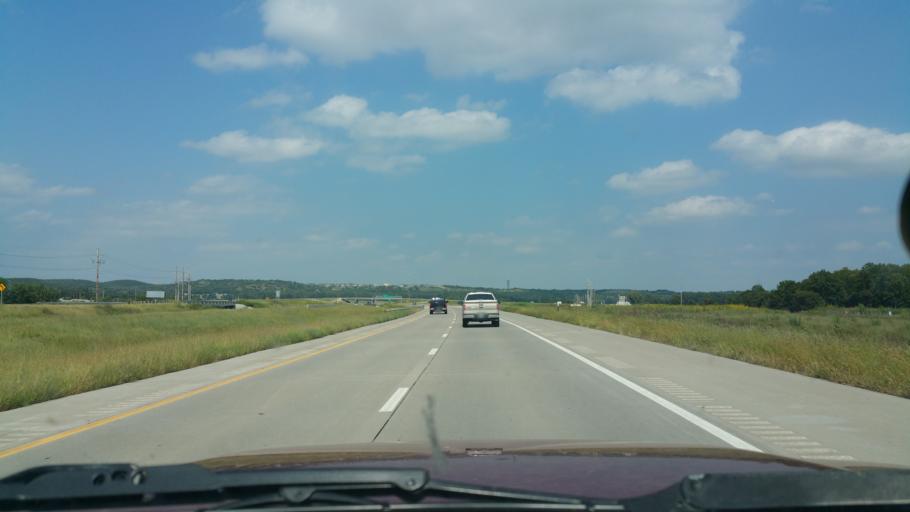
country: US
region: Kansas
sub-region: Riley County
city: Ogden
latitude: 39.1456
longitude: -96.6512
